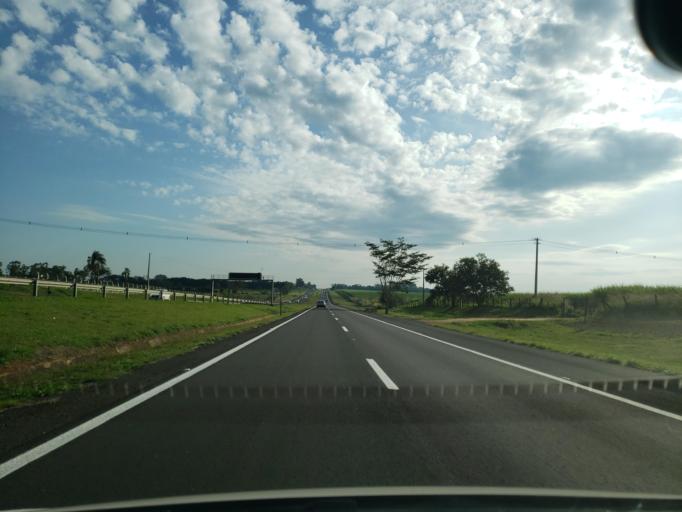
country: BR
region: Sao Paulo
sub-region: Guararapes
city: Guararapes
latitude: -21.2023
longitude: -50.5961
